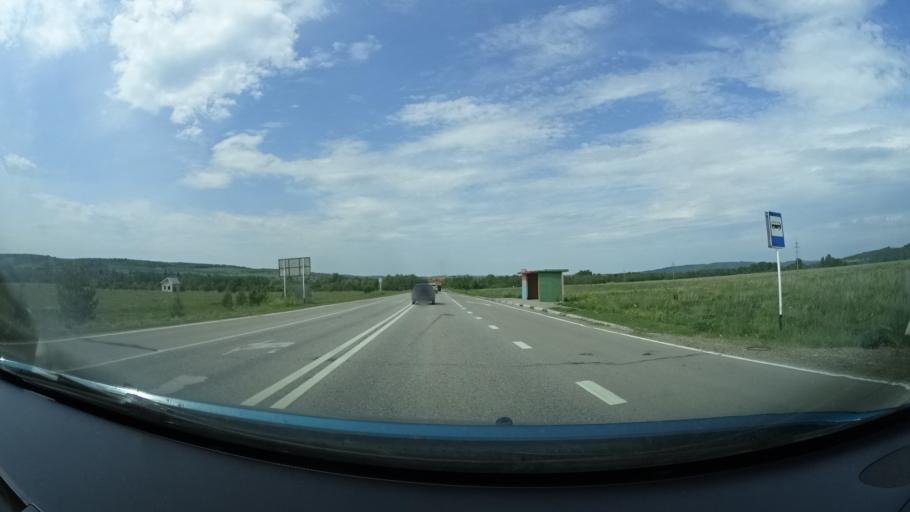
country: RU
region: Perm
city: Barda
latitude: 57.0222
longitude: 55.5552
